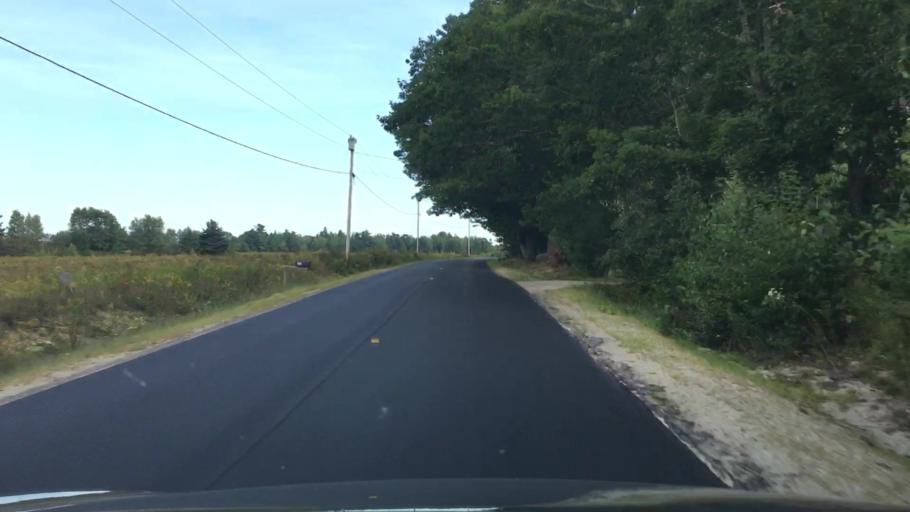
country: US
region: Maine
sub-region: Hancock County
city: Penobscot
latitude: 44.5373
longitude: -68.6150
